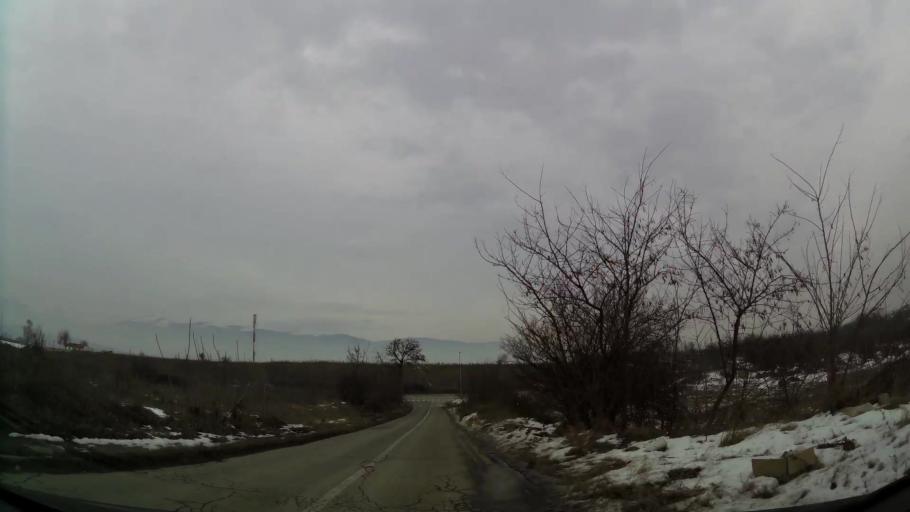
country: MK
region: Butel
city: Butel
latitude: 42.0398
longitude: 21.4384
